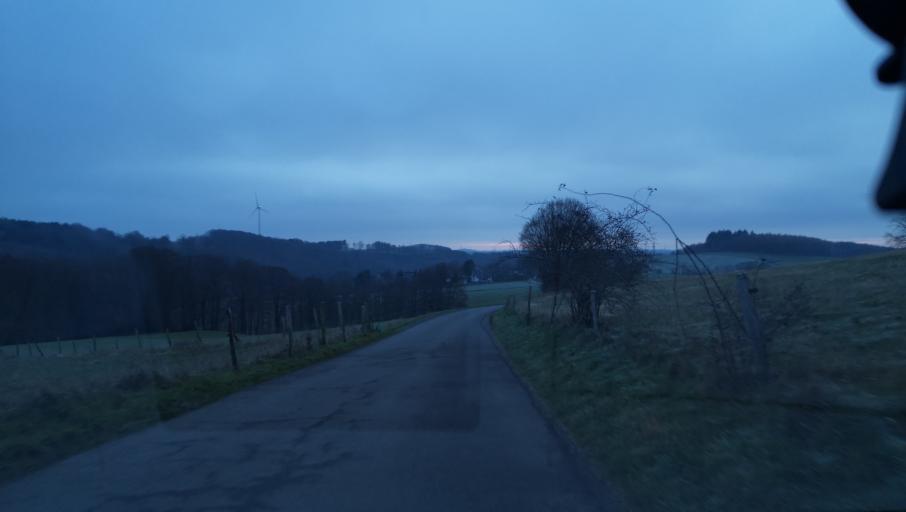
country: DE
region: North Rhine-Westphalia
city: Radevormwald
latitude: 51.1919
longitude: 7.3511
